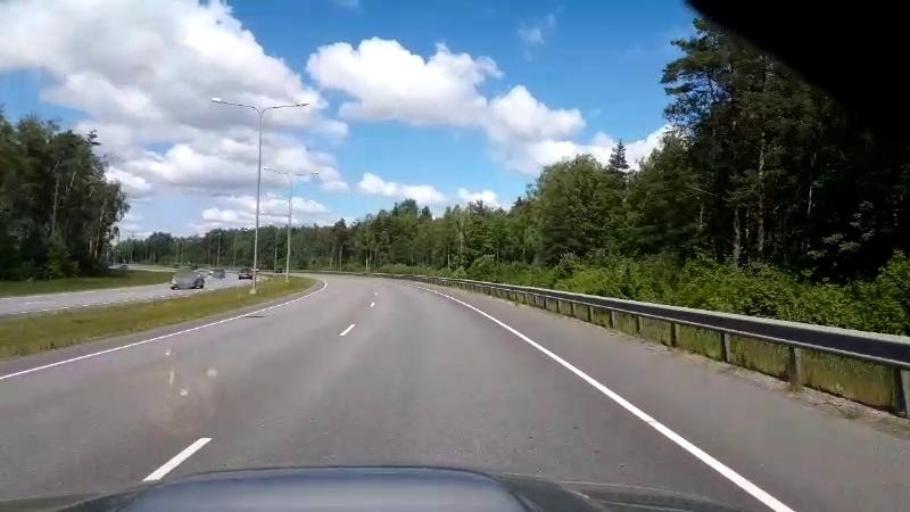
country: EE
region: Paernumaa
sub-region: Paernu linn
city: Parnu
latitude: 58.3869
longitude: 24.5557
